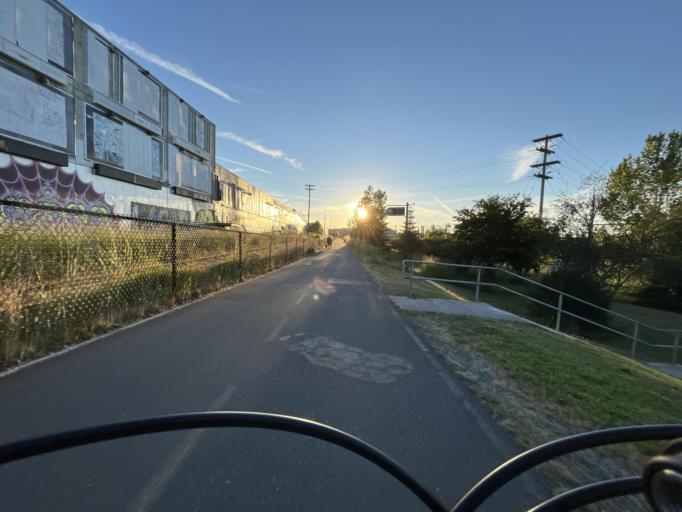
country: CA
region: British Columbia
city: Victoria
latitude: 48.4343
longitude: -123.3941
